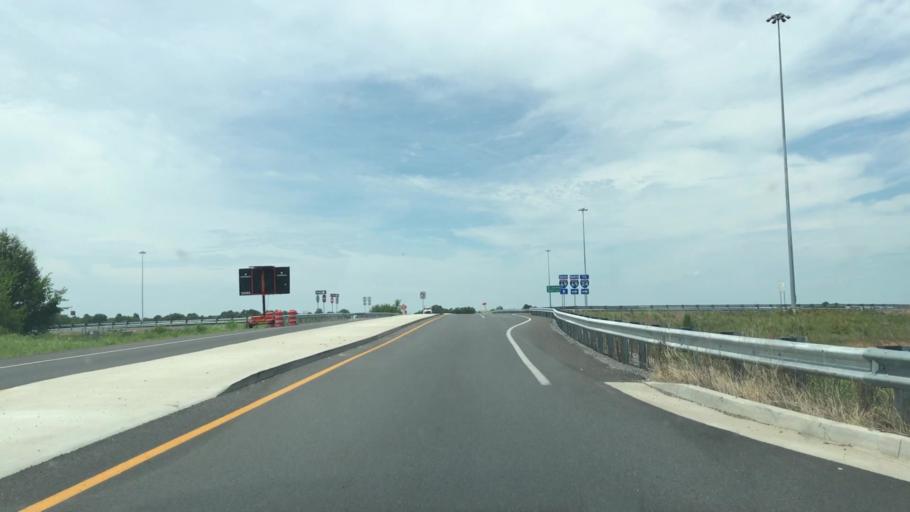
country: US
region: Kentucky
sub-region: Marshall County
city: Benton
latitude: 36.8679
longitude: -88.3625
